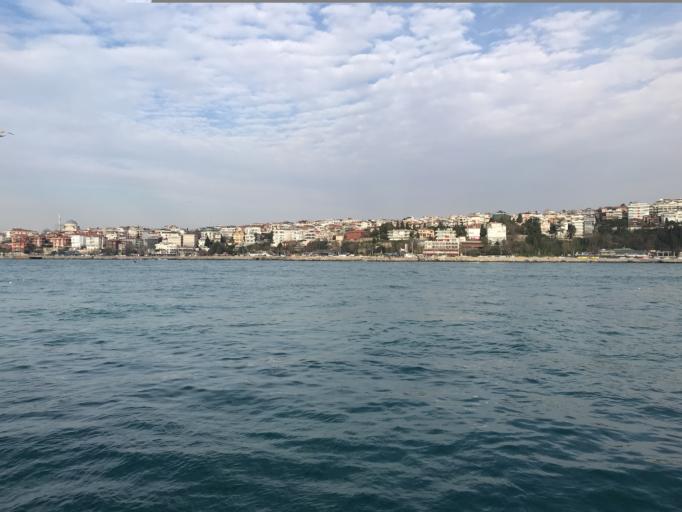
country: TR
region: Istanbul
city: UEskuedar
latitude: 41.0160
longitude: 29.0040
